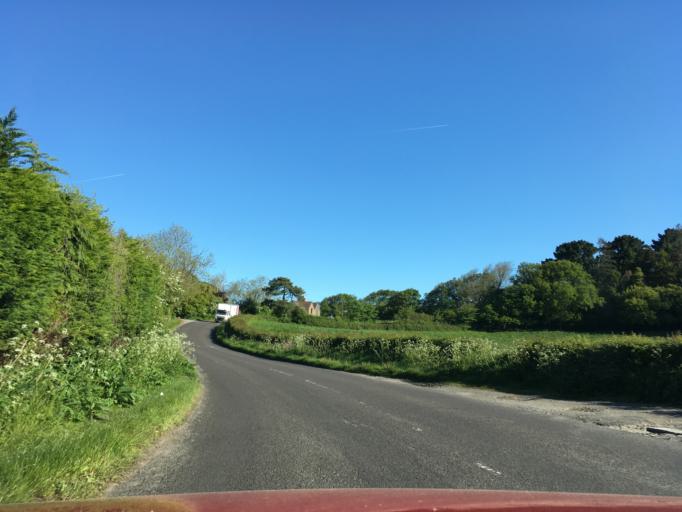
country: GB
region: England
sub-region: North Somerset
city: Clevedon
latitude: 51.4597
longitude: -2.8312
